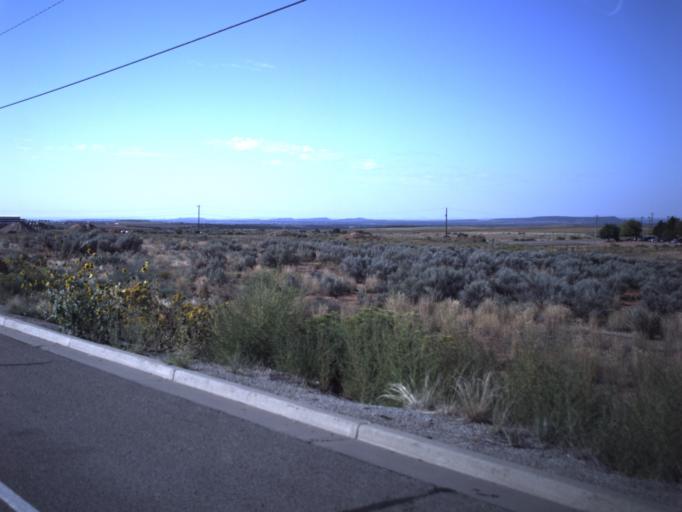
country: US
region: Utah
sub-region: San Juan County
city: Blanding
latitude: 37.6051
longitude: -109.4789
